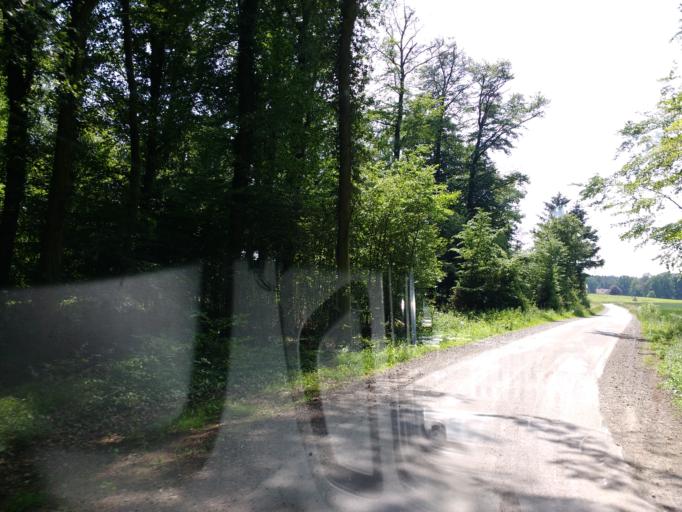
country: DE
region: Lower Saxony
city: Wallenhorst
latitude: 52.3768
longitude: 8.0890
